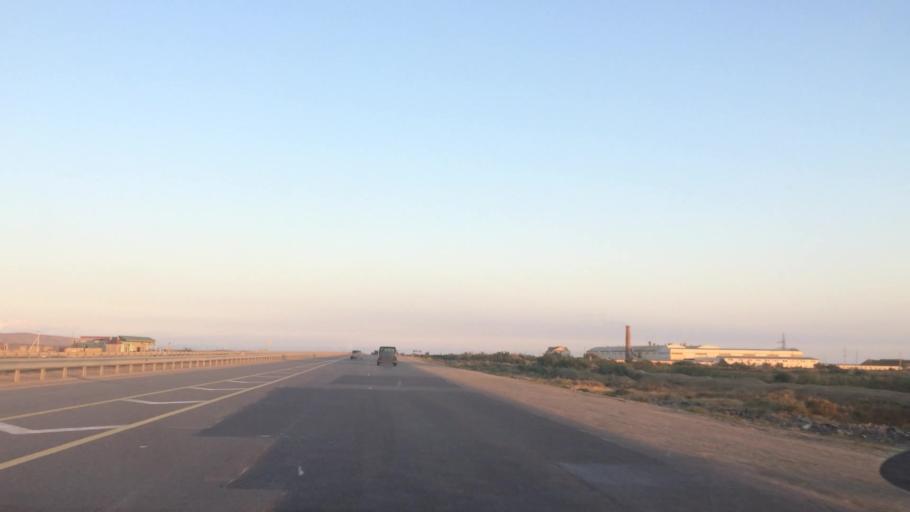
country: AZ
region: Baki
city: Qobustan
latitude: 39.9668
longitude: 49.2741
